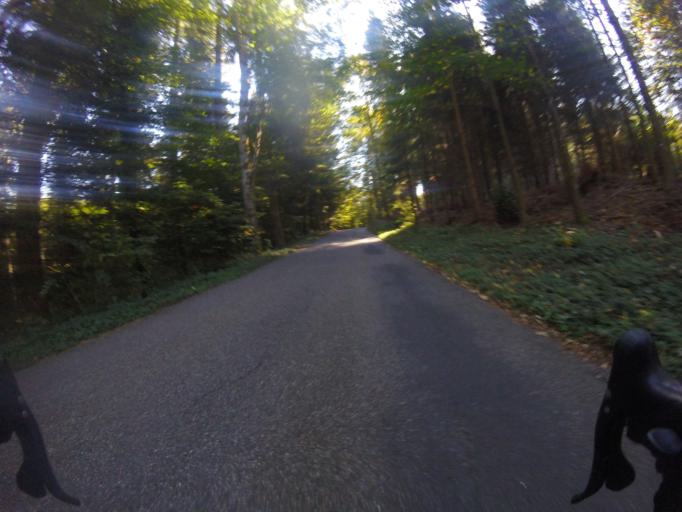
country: CH
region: Bern
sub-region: Seeland District
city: Schupfen
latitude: 47.0332
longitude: 7.3922
